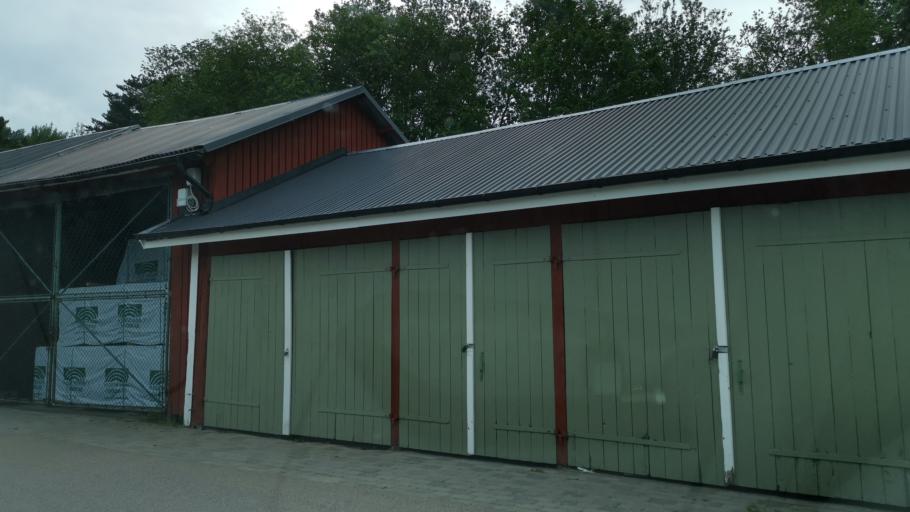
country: SE
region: Vaestra Goetaland
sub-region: Vanersborgs Kommun
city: Vargon
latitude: 58.3443
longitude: 12.3660
